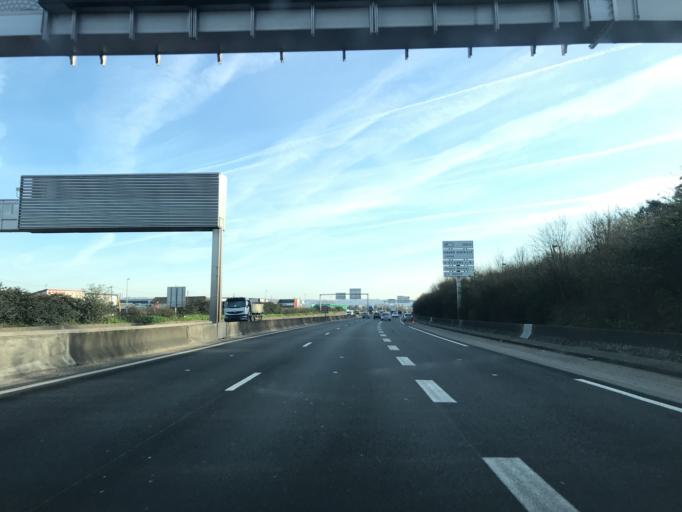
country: FR
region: Haute-Normandie
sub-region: Departement de la Seine-Maritime
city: Le Grand-Quevilly
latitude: 49.4028
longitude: 1.0336
